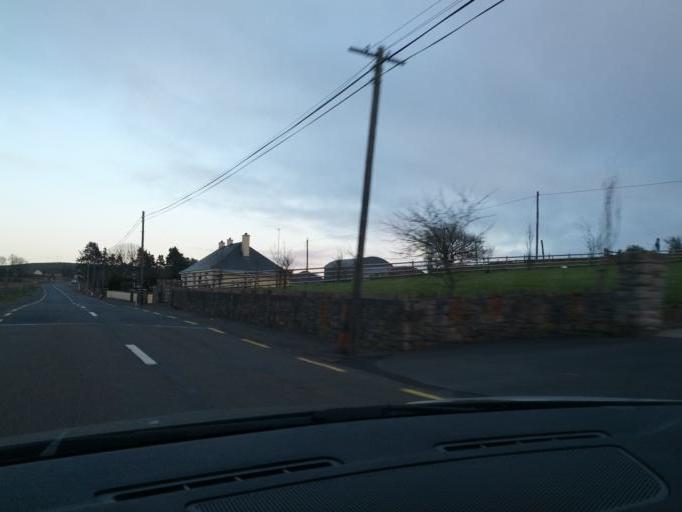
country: IE
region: Connaught
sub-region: Sligo
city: Ballymote
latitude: 53.9855
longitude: -8.4761
